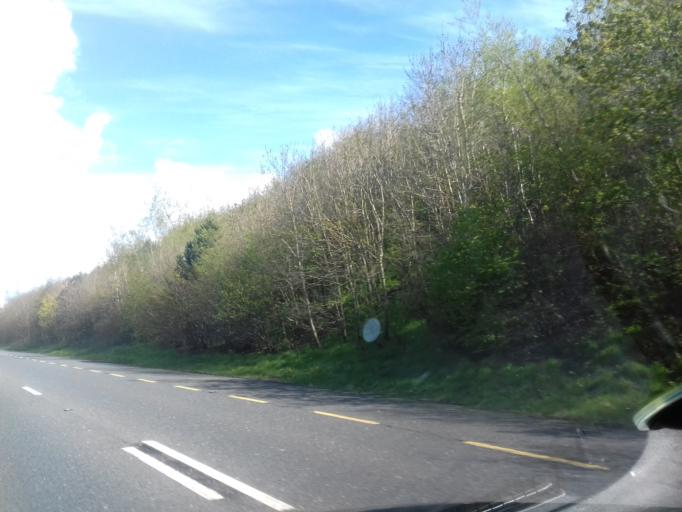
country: IE
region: Ulster
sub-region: An Cabhan
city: Cavan
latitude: 54.0386
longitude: -7.3775
